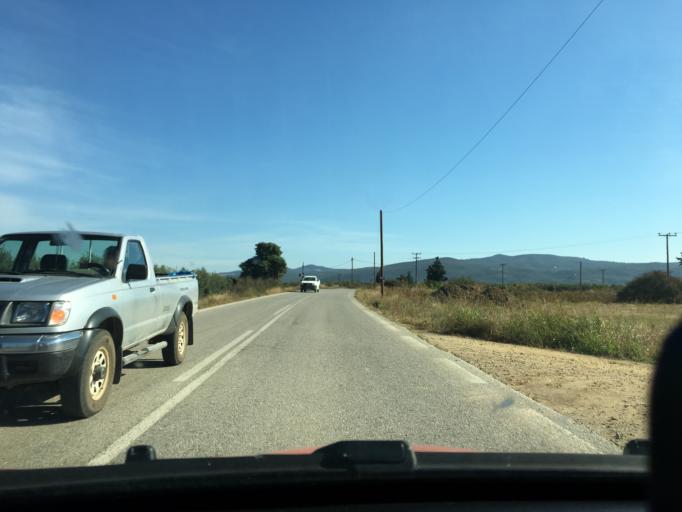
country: GR
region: Central Macedonia
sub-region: Nomos Chalkidikis
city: Ormylia
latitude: 40.2675
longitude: 23.5248
